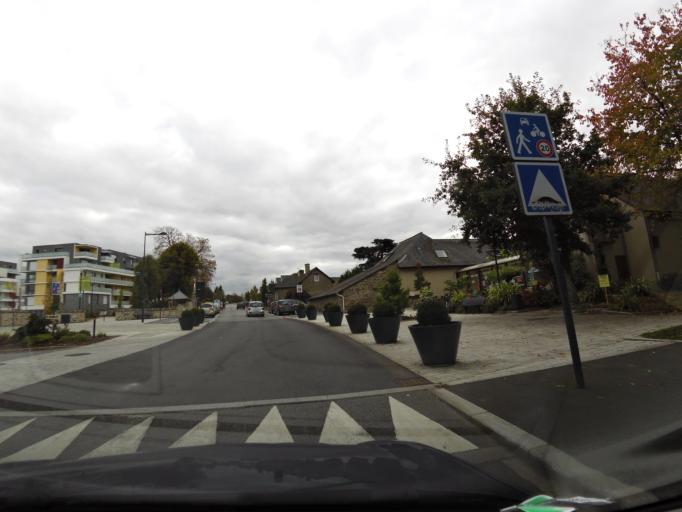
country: FR
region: Brittany
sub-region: Departement d'Ille-et-Vilaine
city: Chantepie
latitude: 48.0873
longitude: -1.6165
